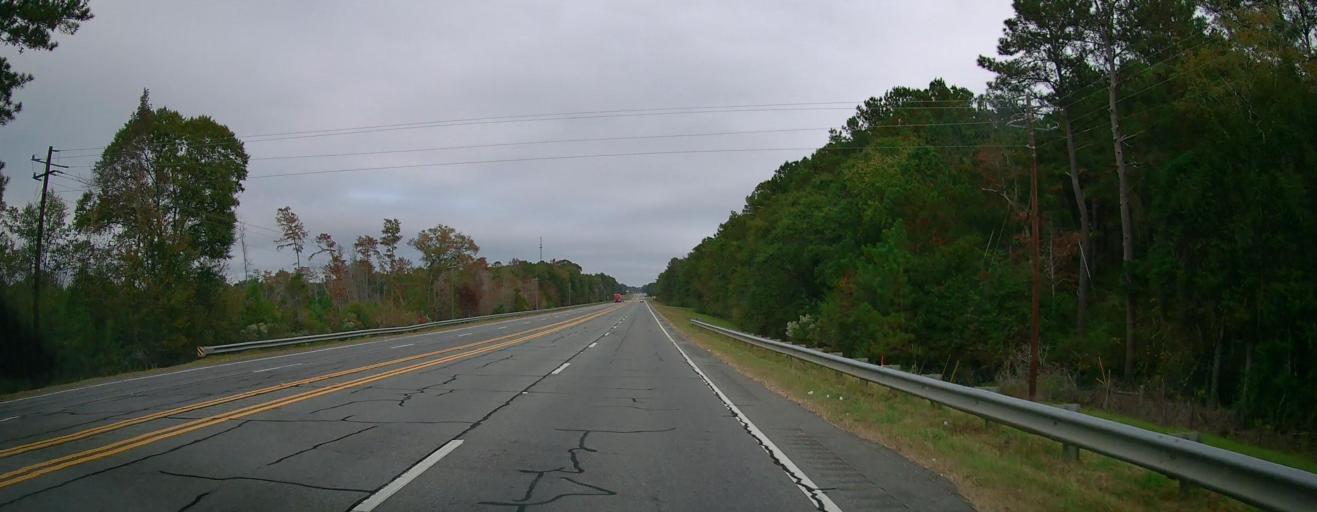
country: US
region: Georgia
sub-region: Tift County
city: Omega
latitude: 31.3189
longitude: -83.6262
